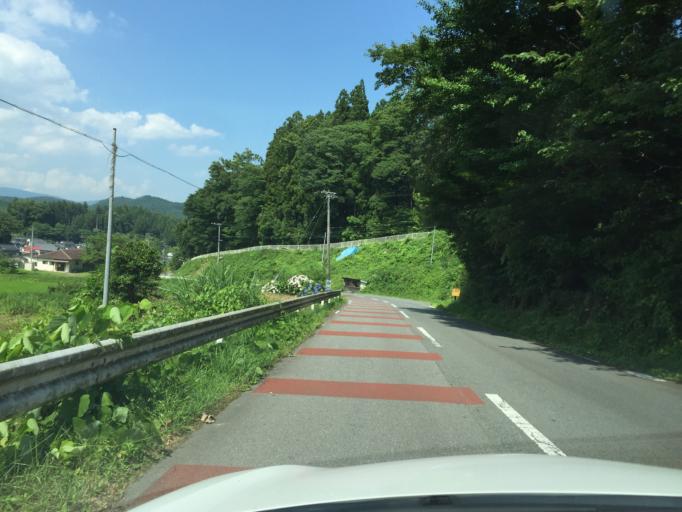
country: JP
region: Ibaraki
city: Kitaibaraki
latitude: 36.9649
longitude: 140.7020
